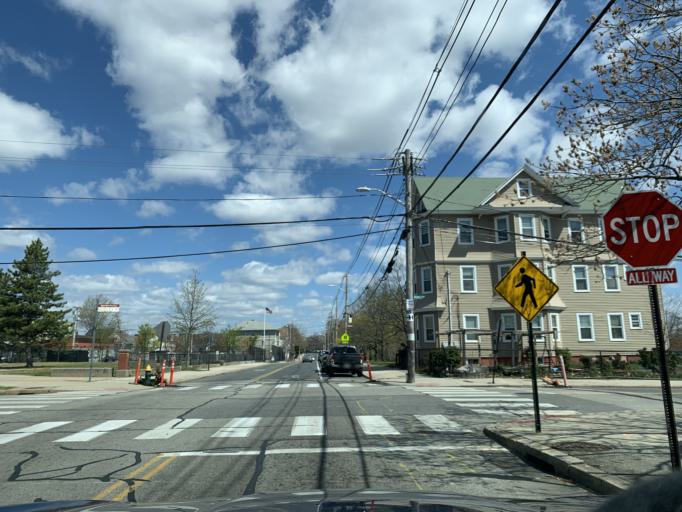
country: US
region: Rhode Island
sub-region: Providence County
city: Providence
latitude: 41.8098
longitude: -71.4157
